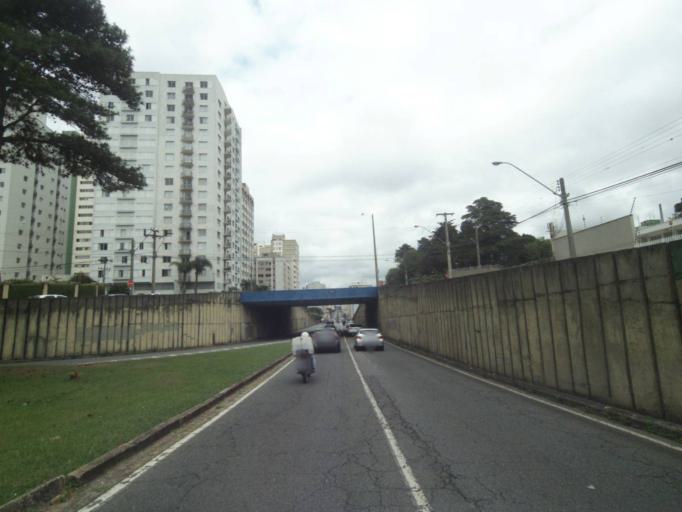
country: BR
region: Parana
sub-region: Curitiba
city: Curitiba
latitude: -25.4318
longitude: -49.2561
